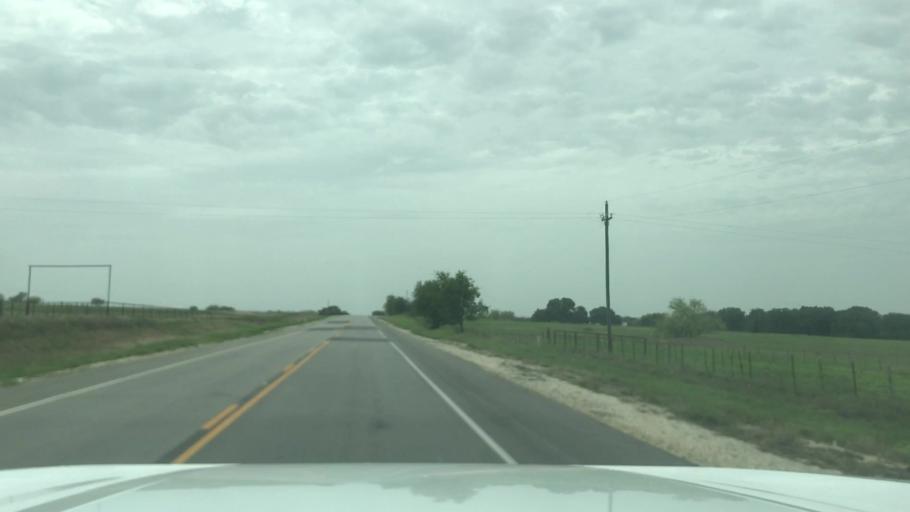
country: US
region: Texas
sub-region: Erath County
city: Dublin
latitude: 32.0666
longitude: -98.2172
